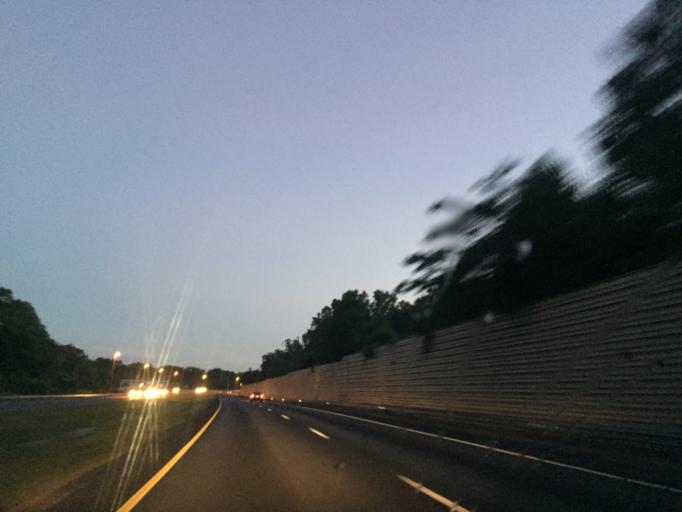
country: US
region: Georgia
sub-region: Chatham County
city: Thunderbolt
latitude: 32.0154
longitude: -81.0849
